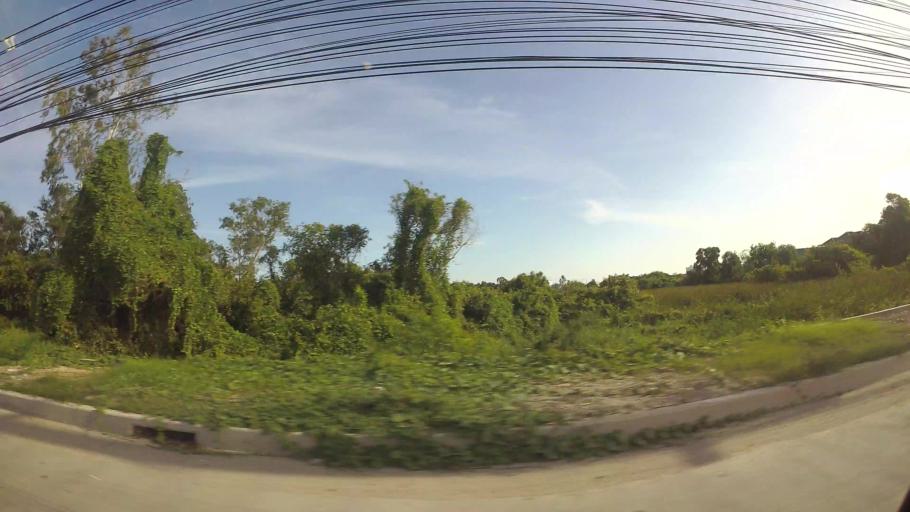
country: TH
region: Rayong
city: Rayong
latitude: 12.6927
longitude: 101.2919
